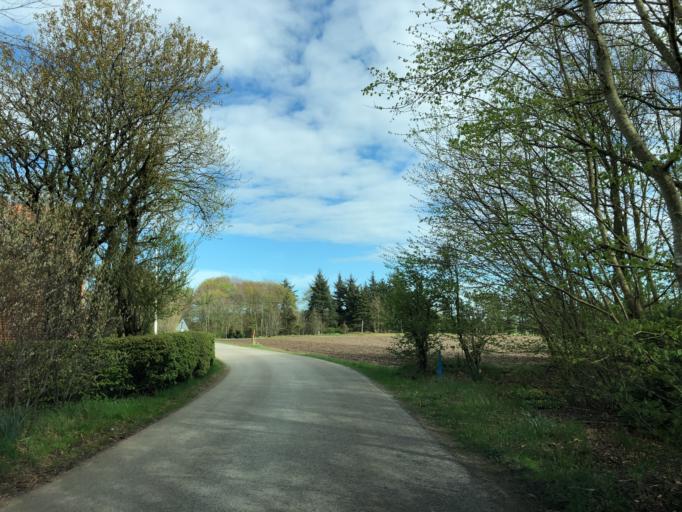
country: DK
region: Central Jutland
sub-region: Holstebro Kommune
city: Ulfborg
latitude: 56.2522
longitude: 8.3230
